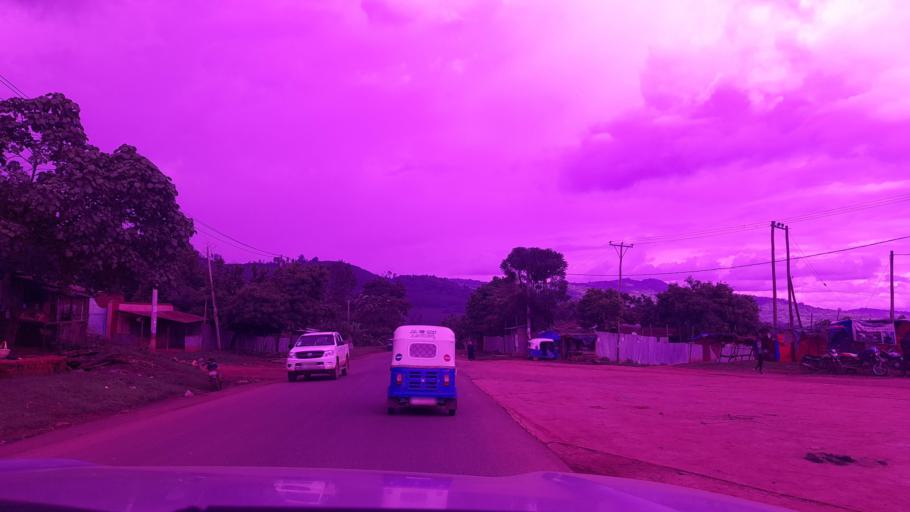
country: ET
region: Oromiya
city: Jima
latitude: 7.6698
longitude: 36.8591
